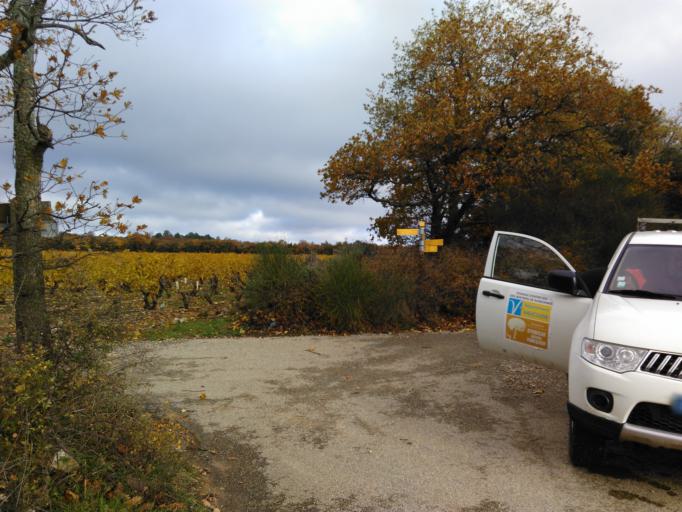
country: FR
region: Rhone-Alpes
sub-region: Departement de la Drome
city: Rochegude
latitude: 44.2262
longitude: 4.8240
